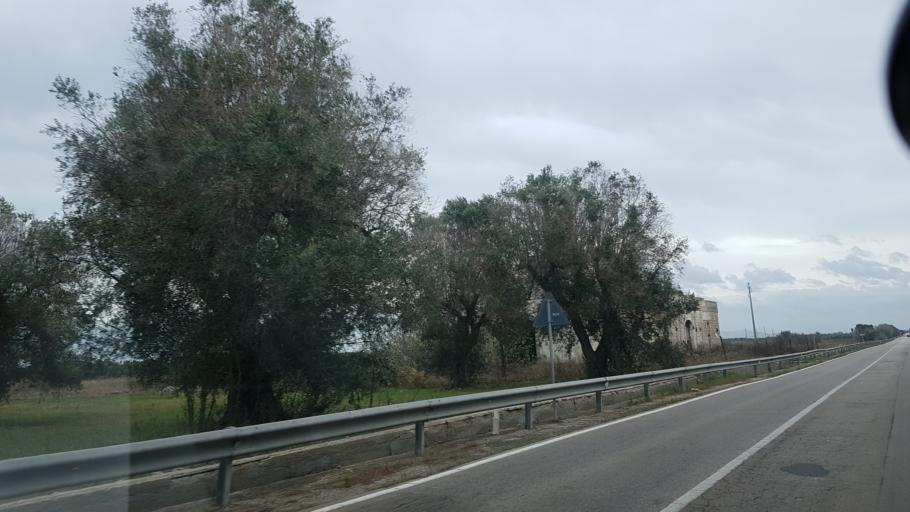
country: IT
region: Apulia
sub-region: Provincia di Brindisi
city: San Donaci
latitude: 40.4061
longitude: 17.8902
